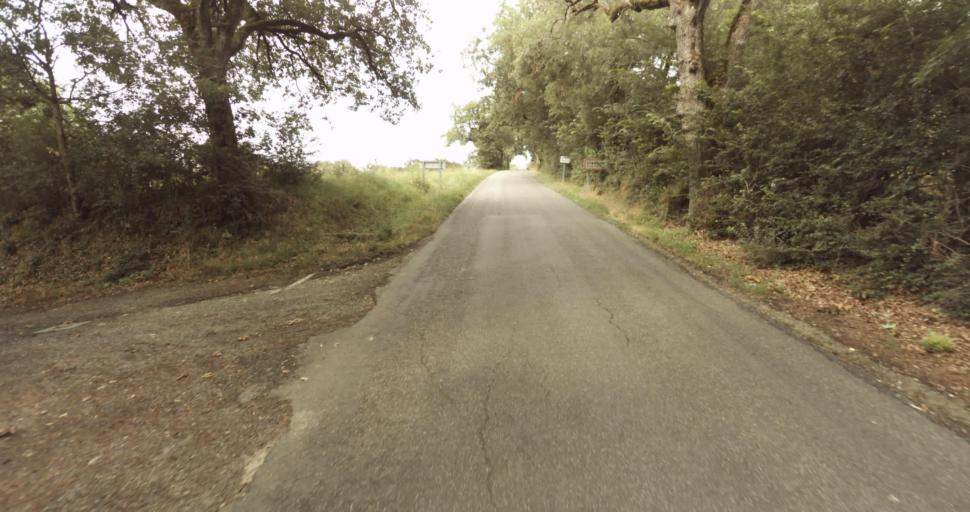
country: FR
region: Midi-Pyrenees
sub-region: Departement de la Haute-Garonne
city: Fontenilles
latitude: 43.5588
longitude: 1.2127
